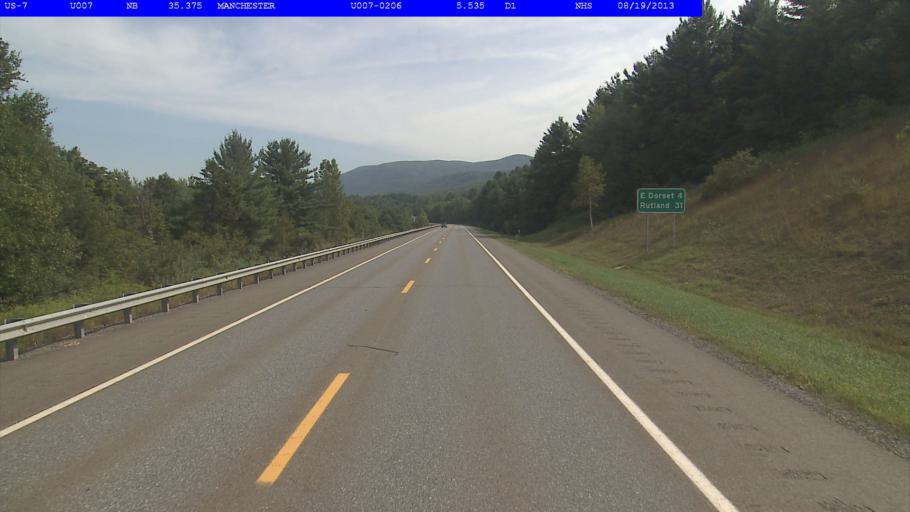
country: US
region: Vermont
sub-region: Bennington County
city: Manchester Center
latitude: 43.1832
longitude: -73.0198
